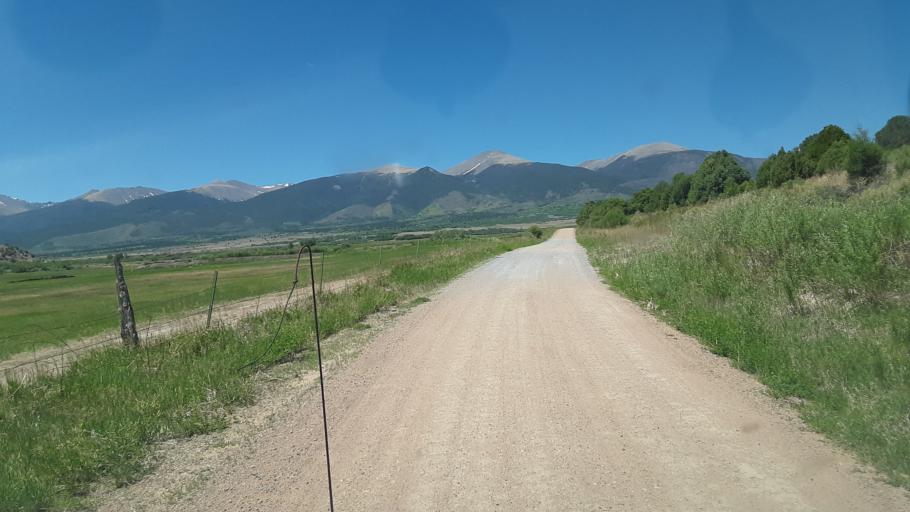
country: US
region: Colorado
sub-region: Custer County
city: Westcliffe
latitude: 38.2950
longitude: -105.6154
